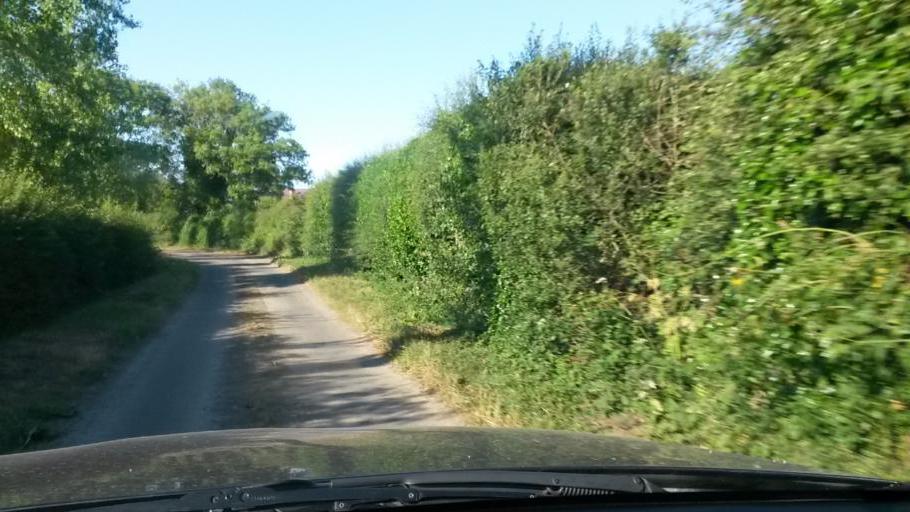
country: IE
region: Leinster
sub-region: Dublin City
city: Finglas
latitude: 53.4467
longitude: -6.3105
